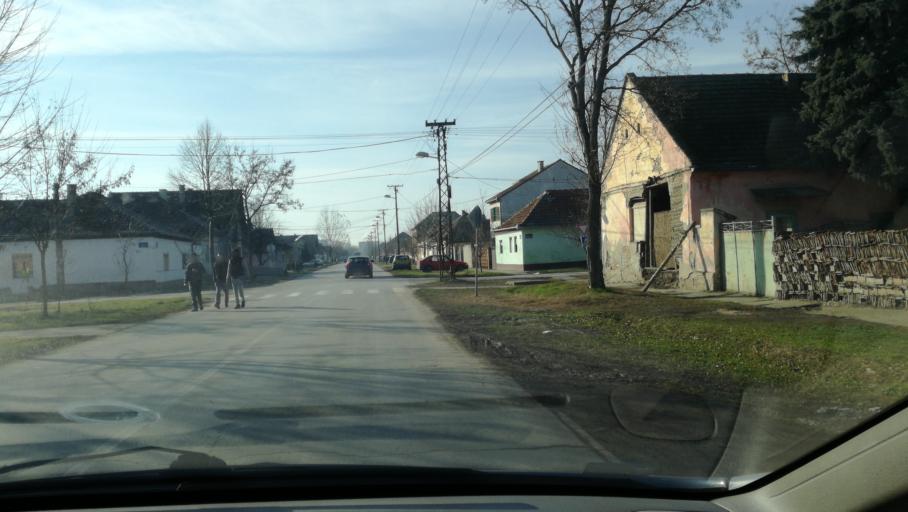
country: RS
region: Autonomna Pokrajina Vojvodina
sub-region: Severnobanatski Okrug
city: Kikinda
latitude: 45.8167
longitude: 20.4633
